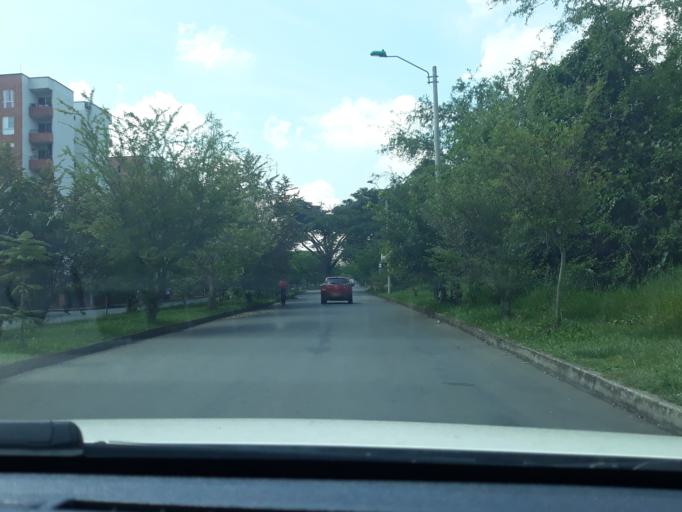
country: CO
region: Valle del Cauca
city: Cali
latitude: 3.3576
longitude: -76.5205
